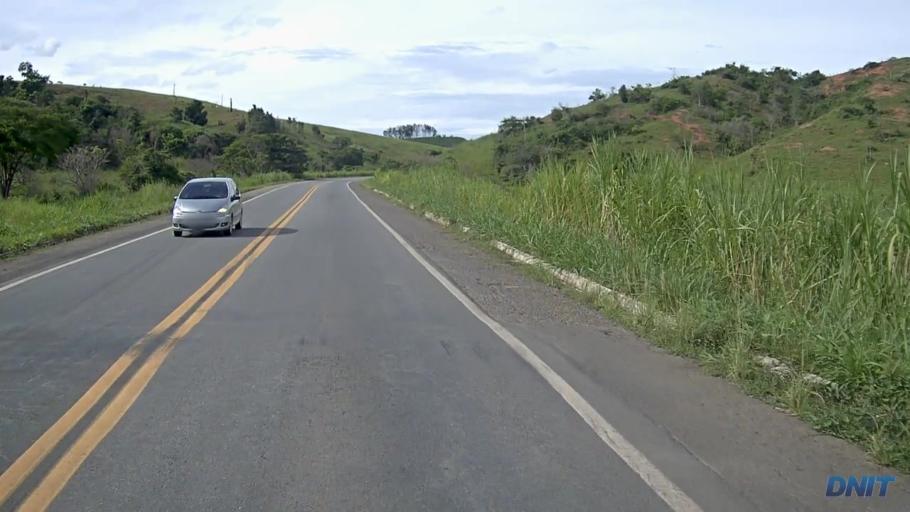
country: BR
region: Minas Gerais
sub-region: Belo Oriente
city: Belo Oriente
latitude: -19.2149
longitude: -42.3065
